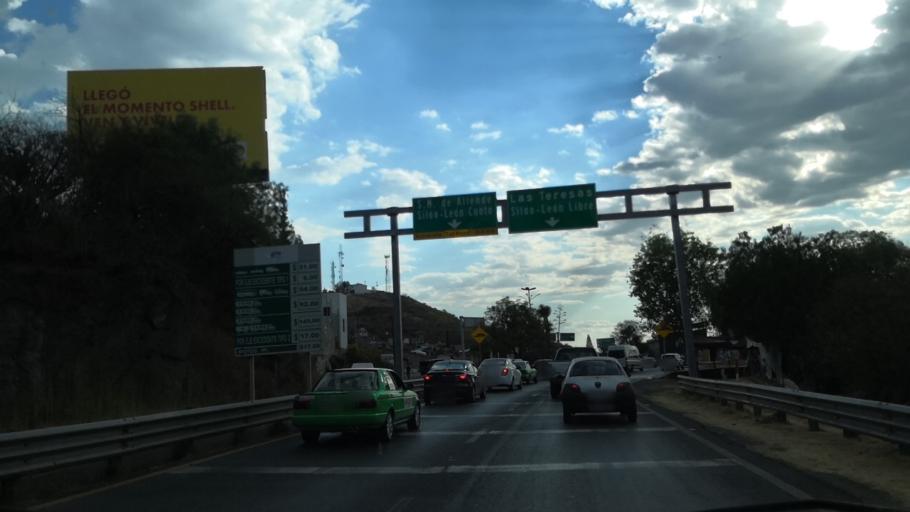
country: MX
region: Guanajuato
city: Marfil
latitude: 20.9983
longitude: -101.2848
